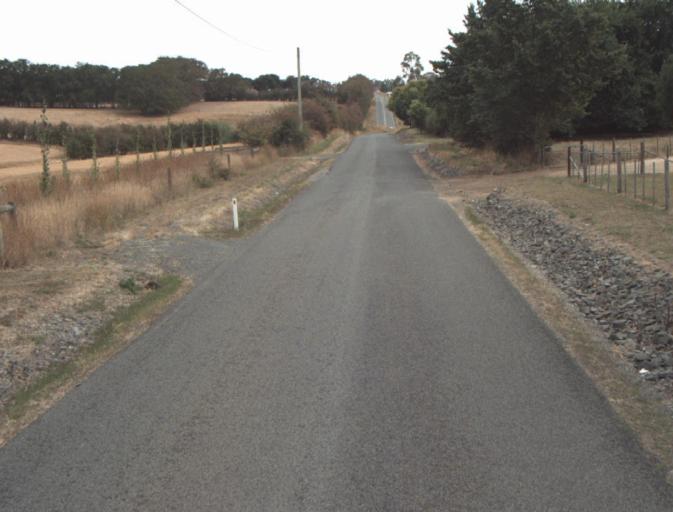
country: AU
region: Tasmania
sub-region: Northern Midlands
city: Evandale
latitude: -41.5056
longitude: 147.2533
